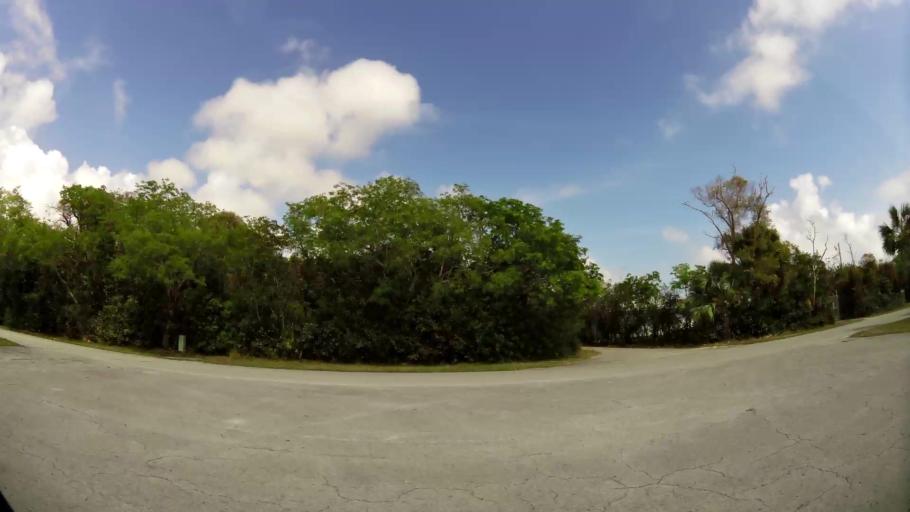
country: BS
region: Freeport
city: Freeport
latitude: 26.5067
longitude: -78.7088
